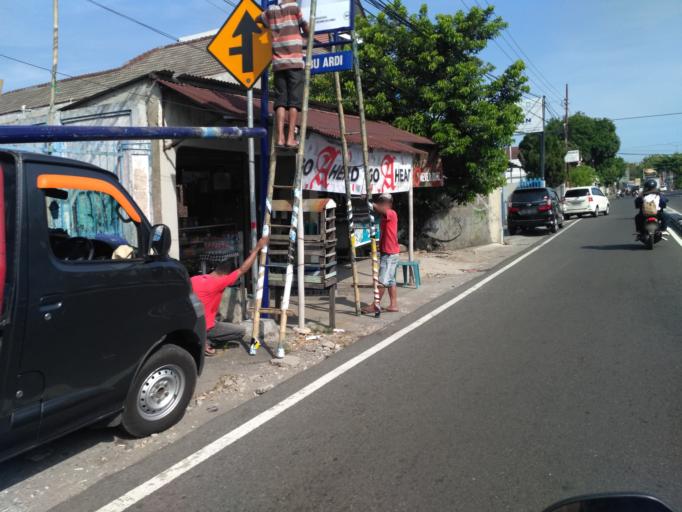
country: ID
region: Daerah Istimewa Yogyakarta
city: Depok
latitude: -7.7811
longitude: 110.4301
